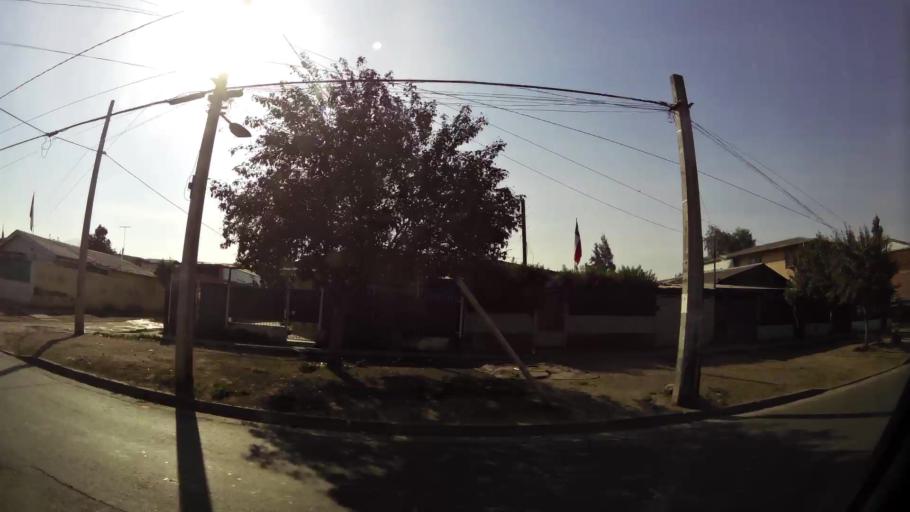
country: CL
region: Santiago Metropolitan
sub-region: Provincia de Santiago
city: Lo Prado
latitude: -33.4160
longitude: -70.7474
